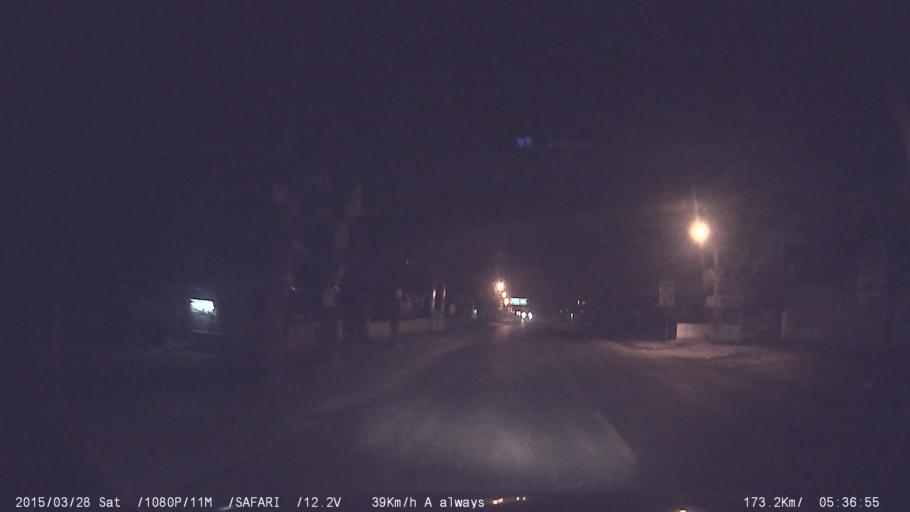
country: IN
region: Karnataka
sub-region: Bangalore Urban
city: Bangalore
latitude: 12.8548
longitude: 77.5887
